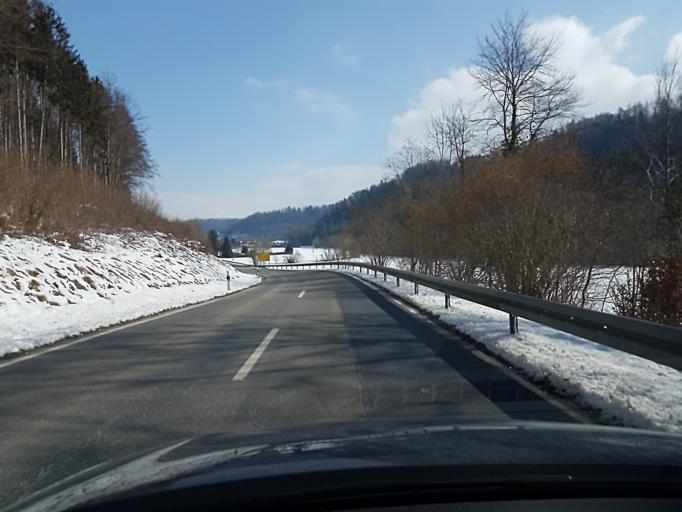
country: DE
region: Baden-Wuerttemberg
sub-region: Freiburg Region
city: Sulz am Neckar
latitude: 48.3556
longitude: 8.6032
